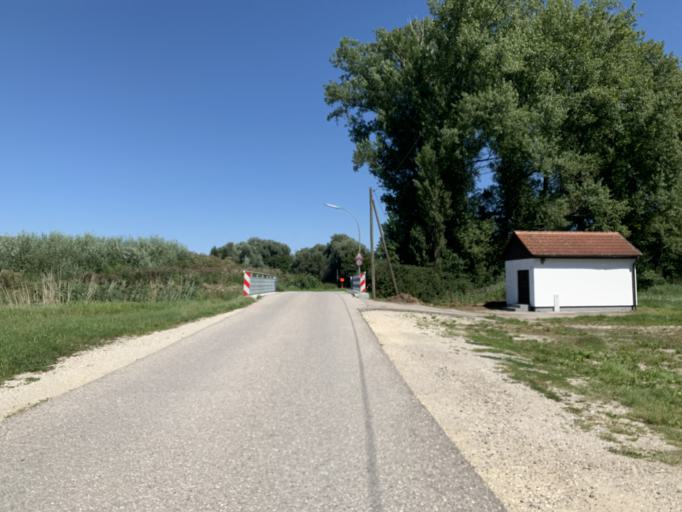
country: DE
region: Bavaria
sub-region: Upper Bavaria
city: Freising
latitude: 48.3917
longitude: 11.7185
